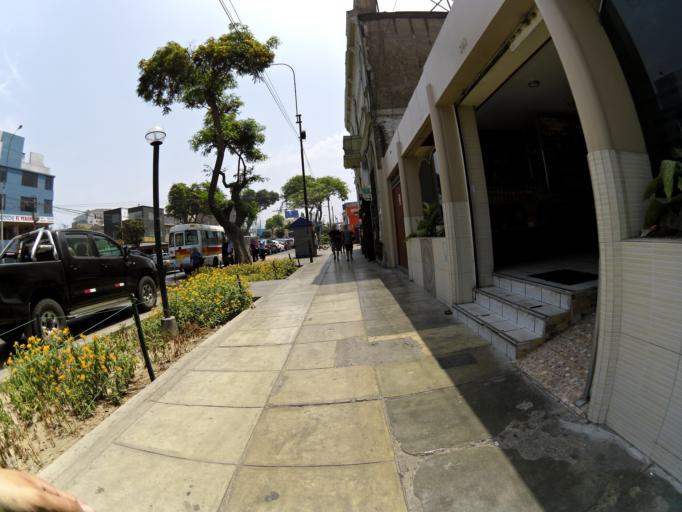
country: PE
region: Lima
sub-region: Lima
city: San Isidro
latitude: -12.1138
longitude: -77.0277
